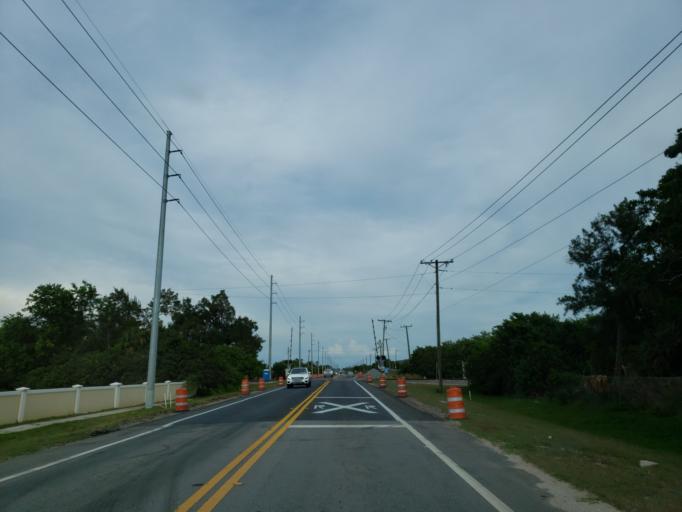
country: US
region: Florida
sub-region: Hillsborough County
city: Ruskin
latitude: 27.7350
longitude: -82.4130
